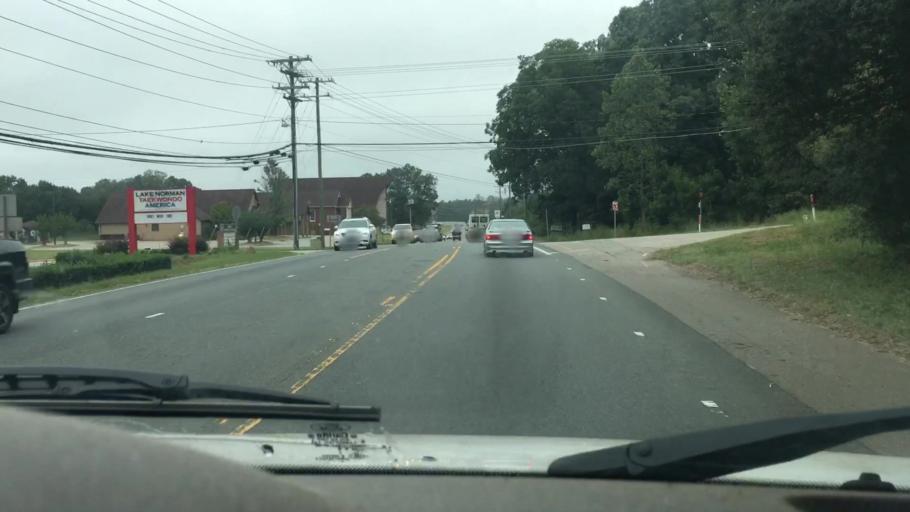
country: US
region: North Carolina
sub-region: Catawba County
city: Lake Norman of Catawba
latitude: 35.6022
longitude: -80.8980
